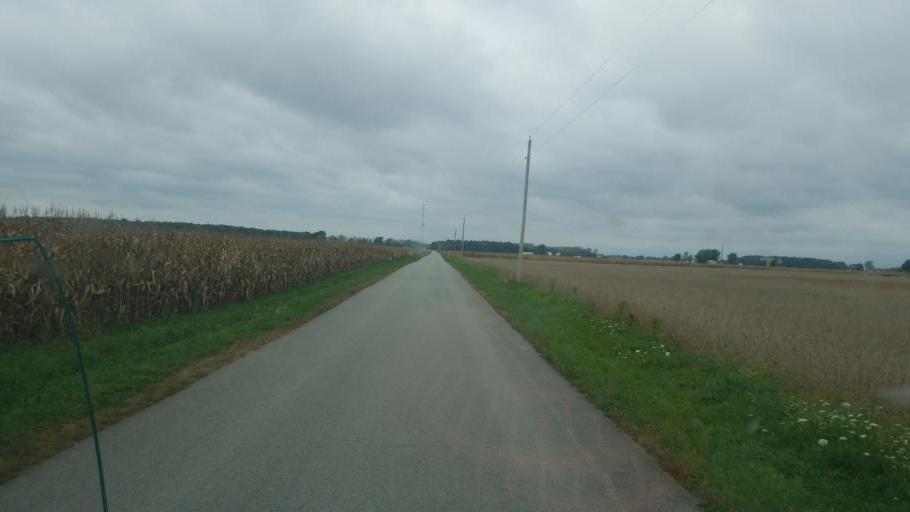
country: US
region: Ohio
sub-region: Seneca County
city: Fostoria
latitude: 41.0792
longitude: -83.5020
